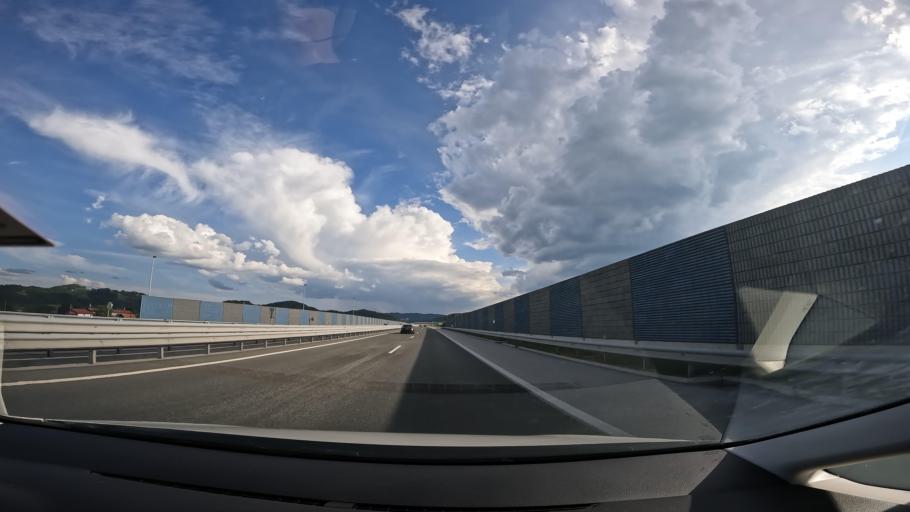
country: SI
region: Podlehnik
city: Podlehnik
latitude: 46.3671
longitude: 15.8664
